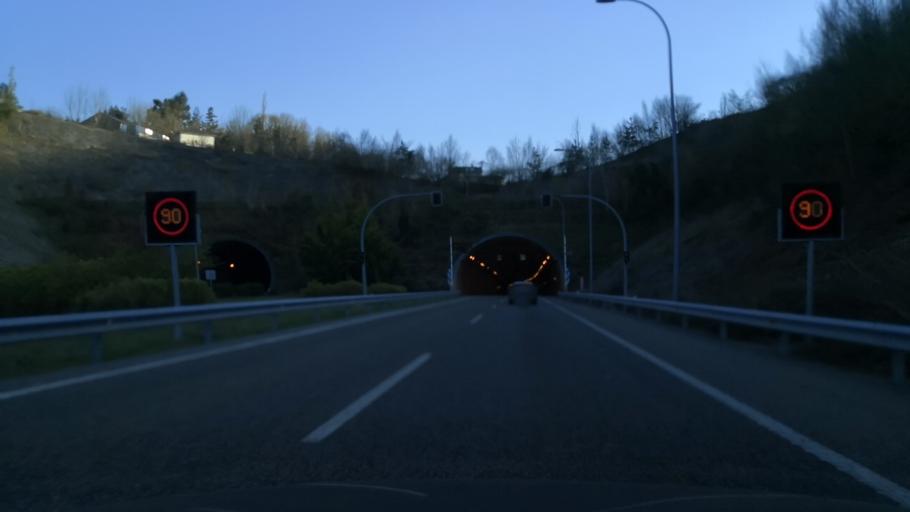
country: ES
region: Galicia
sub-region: Provincia de Lugo
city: Becerrea
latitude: 42.8749
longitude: -7.1762
